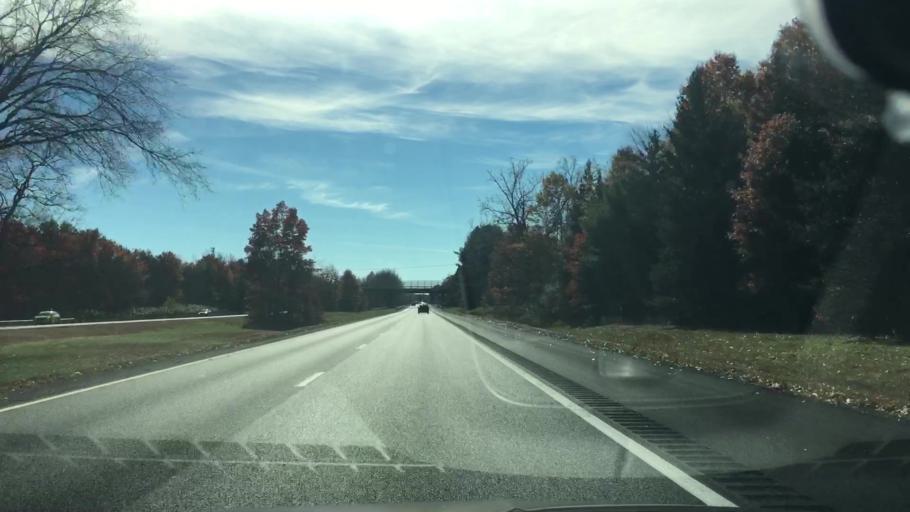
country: US
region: Massachusetts
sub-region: Hampshire County
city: Hatfield
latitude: 42.3847
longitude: -72.6312
